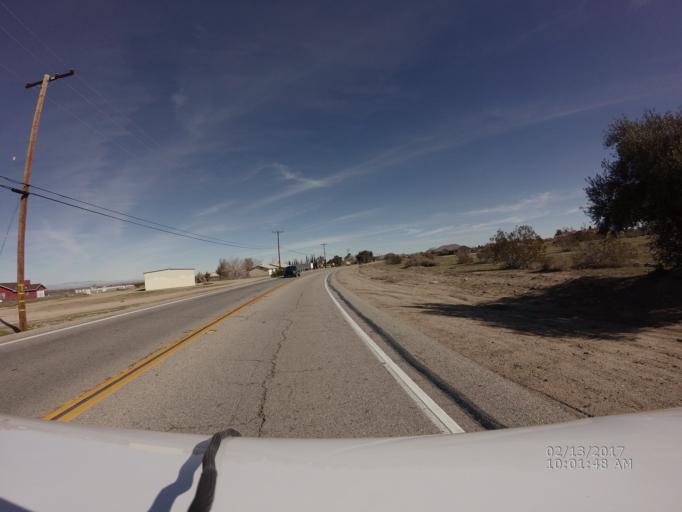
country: US
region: California
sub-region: Los Angeles County
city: Littlerock
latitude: 34.5513
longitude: -117.9745
